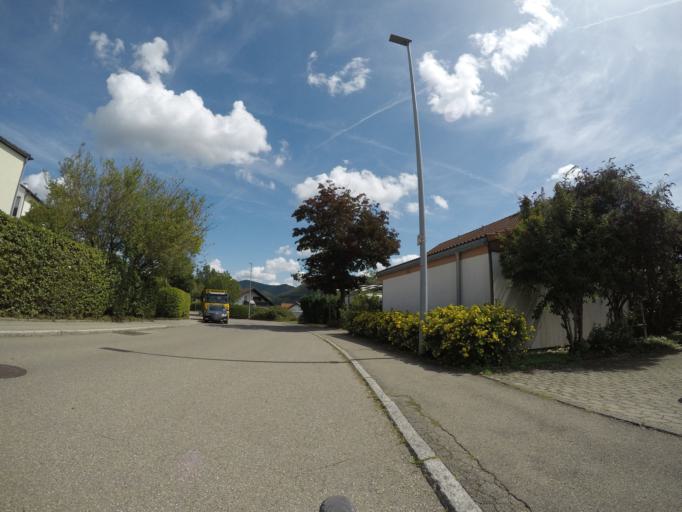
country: DE
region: Baden-Wuerttemberg
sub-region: Tuebingen Region
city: Eningen unter Achalm
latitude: 48.4866
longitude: 9.2492
